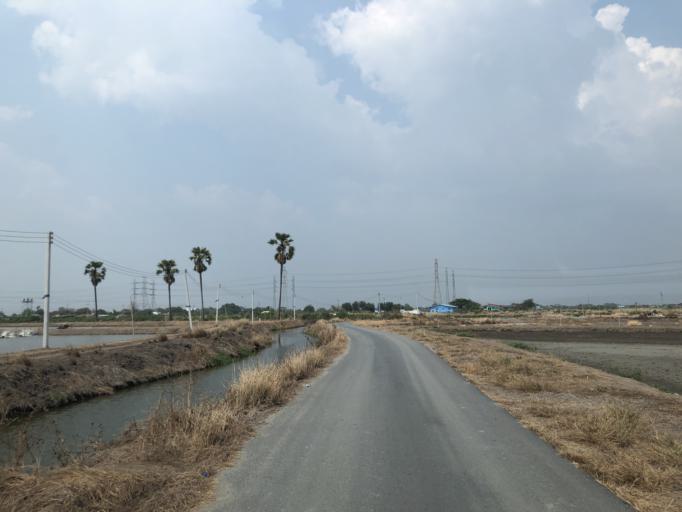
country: TH
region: Samut Prakan
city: Bang Bo
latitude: 13.5412
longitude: 100.8804
